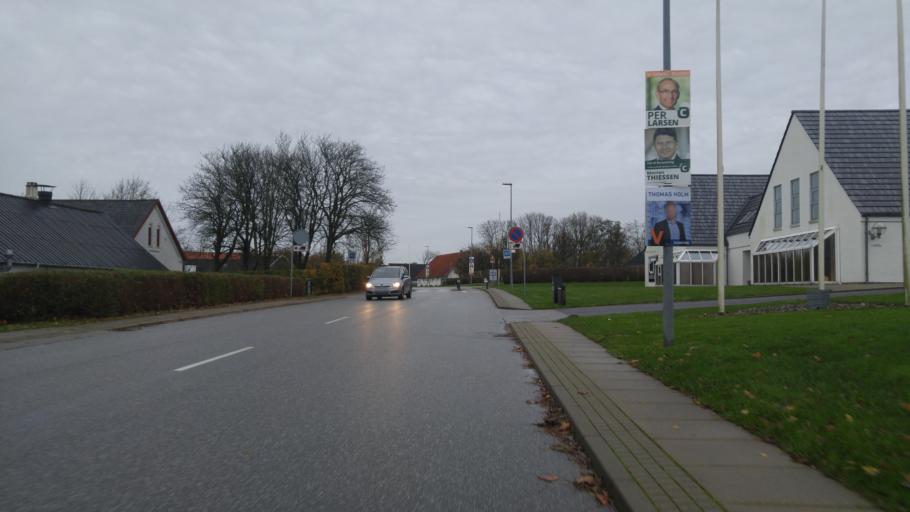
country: DK
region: North Denmark
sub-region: Alborg Kommune
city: Aalborg
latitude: 57.0185
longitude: 9.8818
